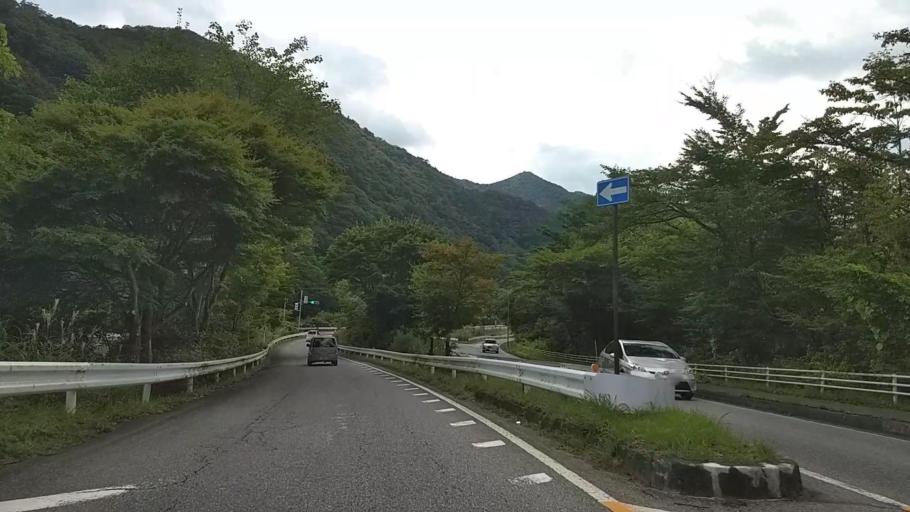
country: JP
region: Tochigi
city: Nikko
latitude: 36.7425
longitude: 139.5668
